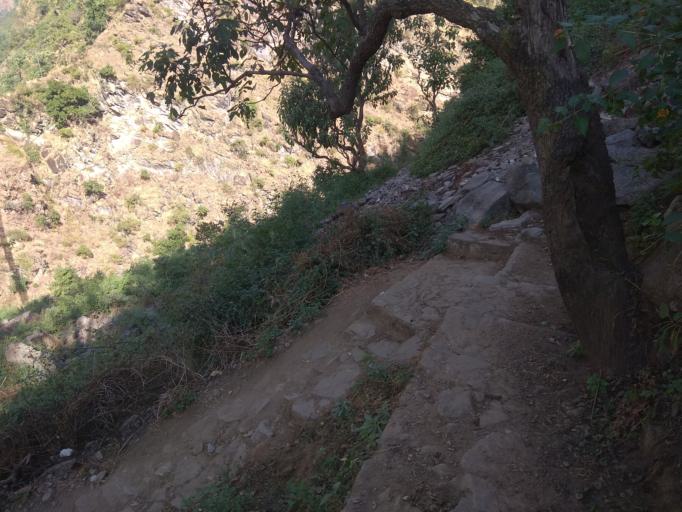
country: NP
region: Far Western
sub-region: Seti Zone
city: Achham
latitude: 29.1346
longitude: 81.5802
